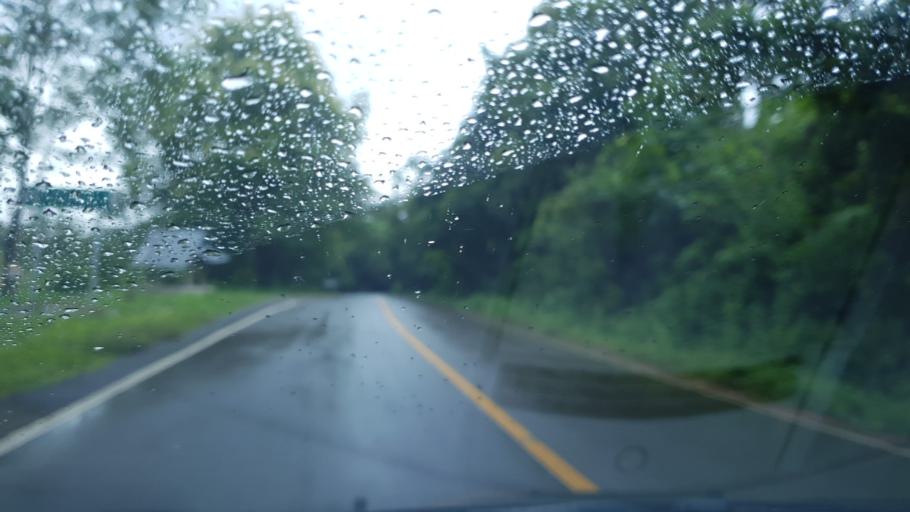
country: TH
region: Mae Hong Son
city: Mae La Noi
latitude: 18.5384
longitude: 97.9375
